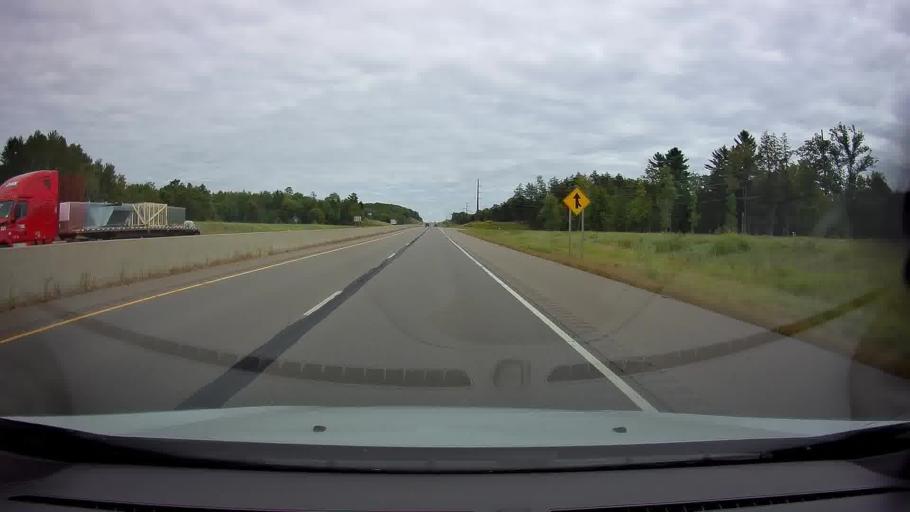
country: US
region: Wisconsin
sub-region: Marathon County
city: Marathon
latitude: 44.9440
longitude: -89.7834
